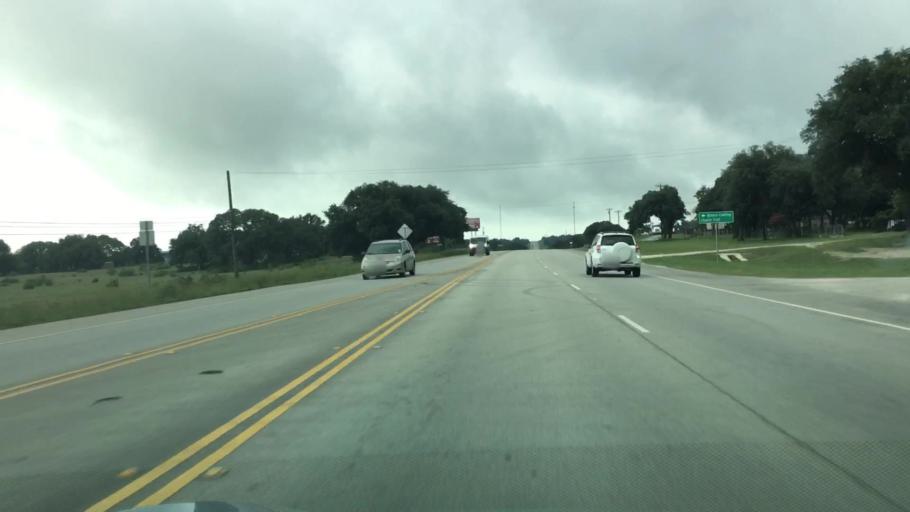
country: US
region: Texas
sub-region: Blanco County
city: Blanco
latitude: 30.0672
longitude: -98.4110
